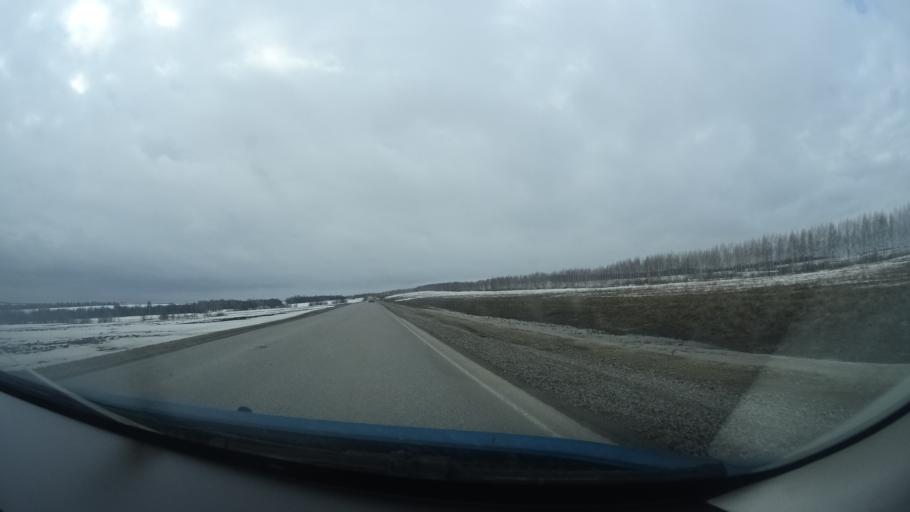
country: RU
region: Bashkortostan
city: Birsk
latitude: 55.3819
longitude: 55.5800
